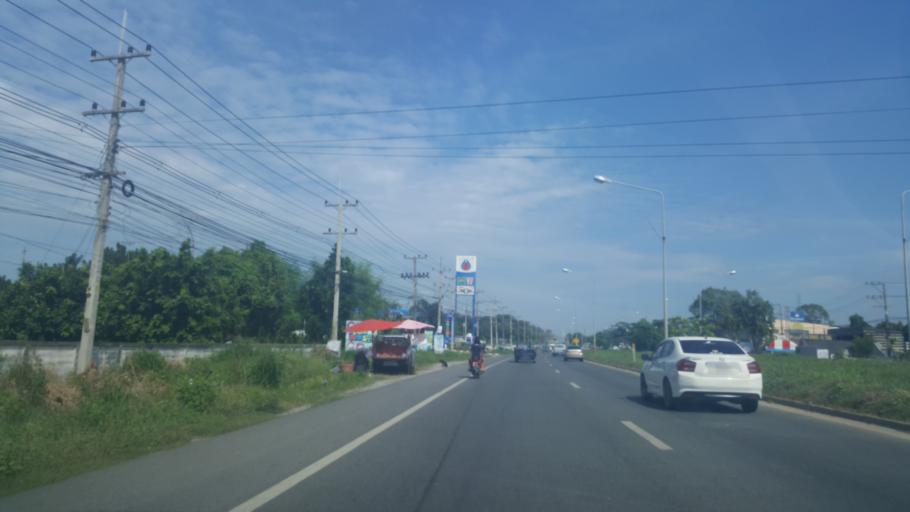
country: TH
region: Chon Buri
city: Sattahip
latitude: 12.6798
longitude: 100.8940
